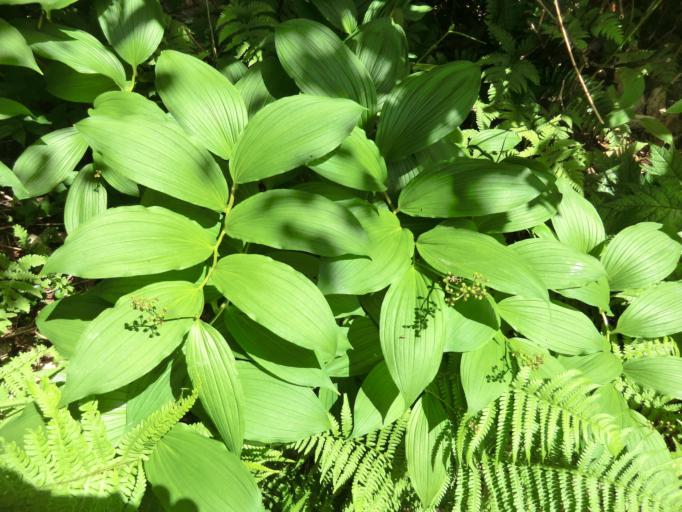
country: JP
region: Gunma
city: Numata
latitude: 36.8874
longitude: 139.1762
